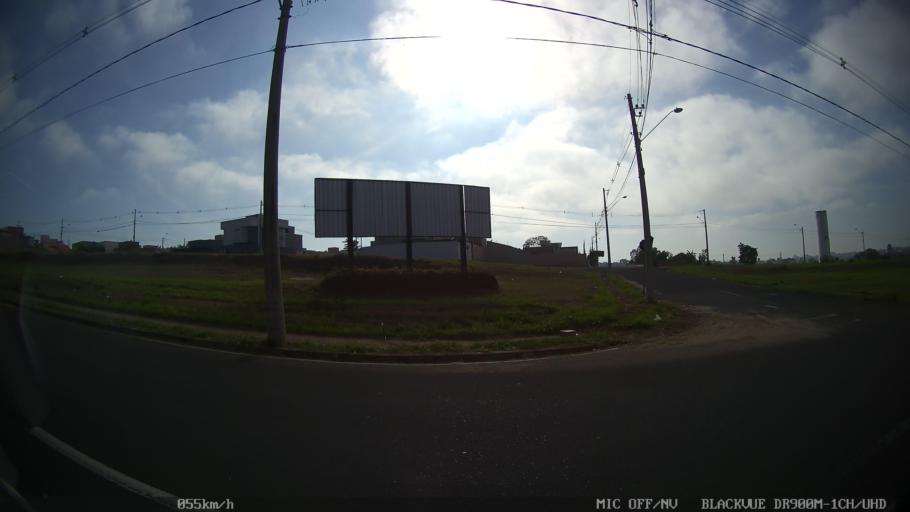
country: BR
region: Sao Paulo
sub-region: Sao Jose Do Rio Preto
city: Sao Jose do Rio Preto
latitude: -20.8034
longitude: -49.4282
